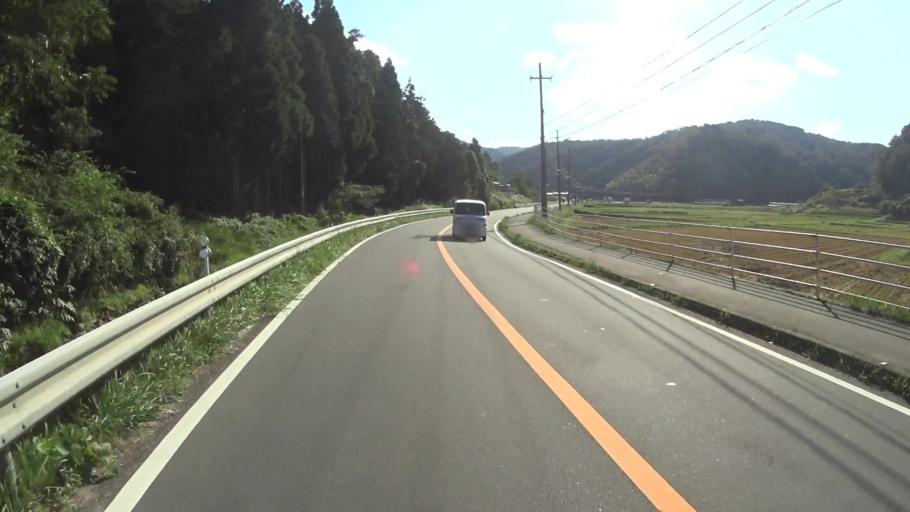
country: JP
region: Kyoto
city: Miyazu
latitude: 35.6624
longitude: 135.0234
